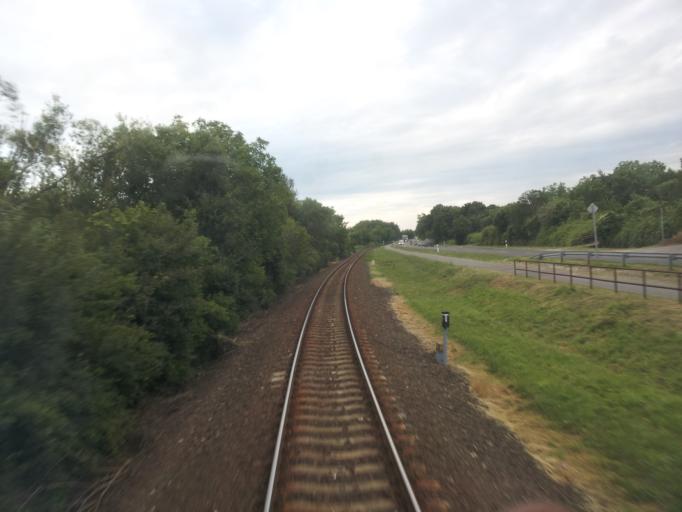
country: HU
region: Veszprem
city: Balatonalmadi
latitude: 47.0028
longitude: 18.0015
